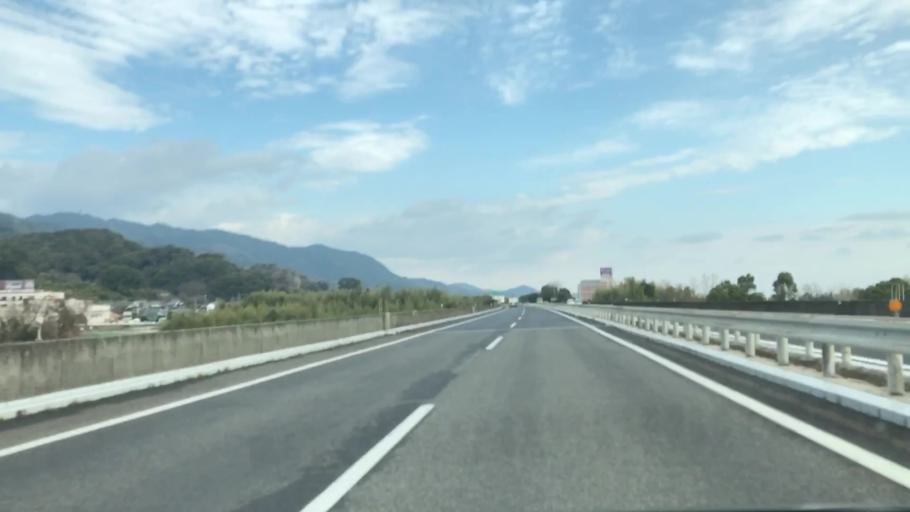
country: JP
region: Saga Prefecture
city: Saga-shi
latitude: 33.3180
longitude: 130.2677
